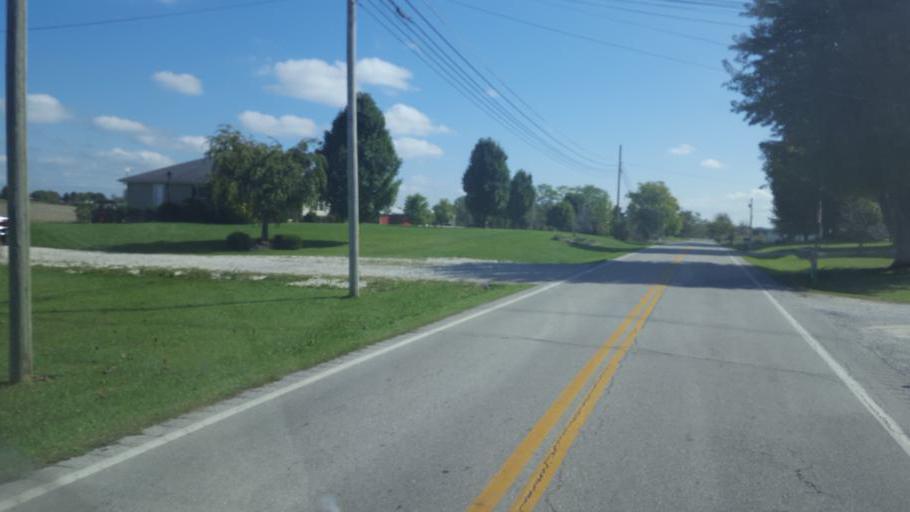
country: US
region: Kentucky
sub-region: Mason County
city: Maysville
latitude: 38.5836
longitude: -83.6532
